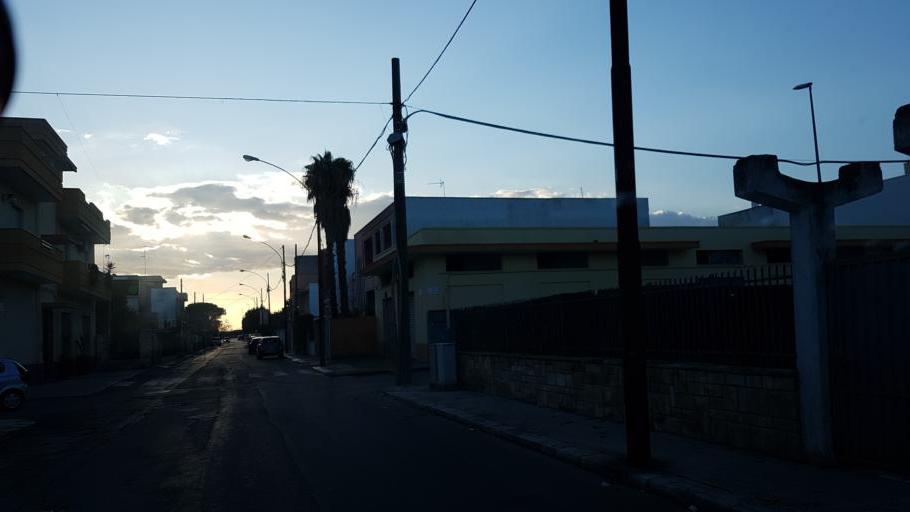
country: IT
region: Apulia
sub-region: Provincia di Lecce
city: Surbo
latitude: 40.3920
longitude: 18.1278
